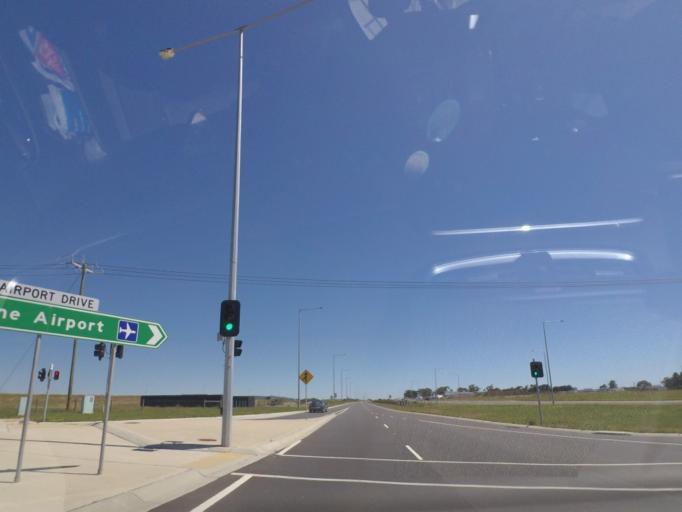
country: AU
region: Victoria
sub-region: Hume
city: Tullamarine
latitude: -37.6924
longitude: 144.8660
